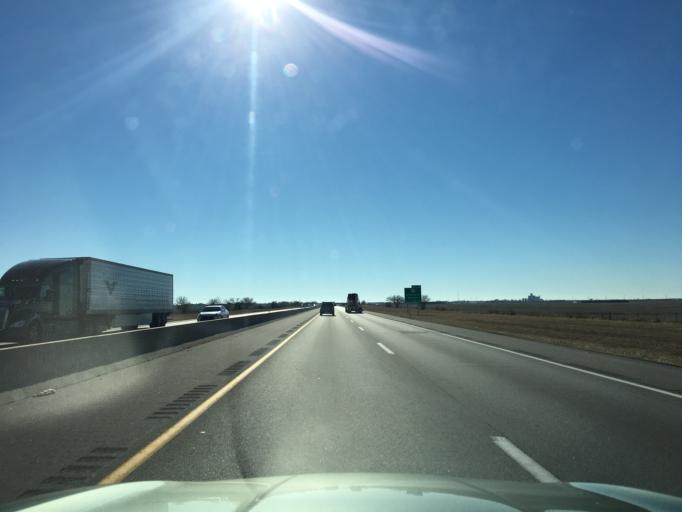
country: US
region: Kansas
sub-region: Sumner County
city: Wellington
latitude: 37.2997
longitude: -97.3404
